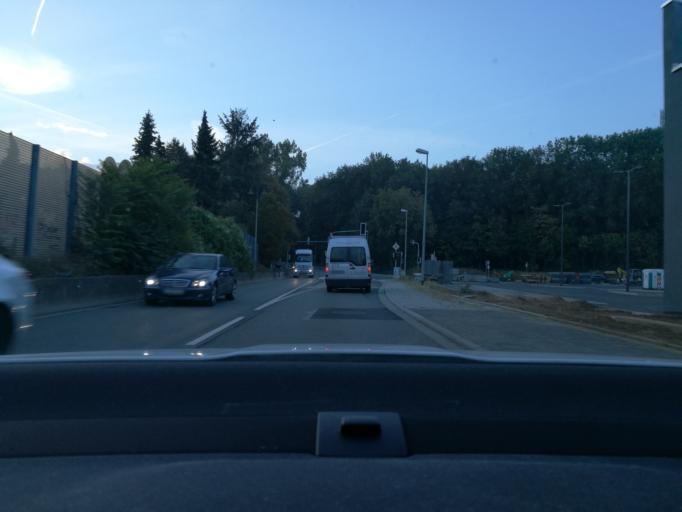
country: DE
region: Hesse
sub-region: Regierungsbezirk Giessen
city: Limburg an der Lahn
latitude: 50.3811
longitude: 8.0753
